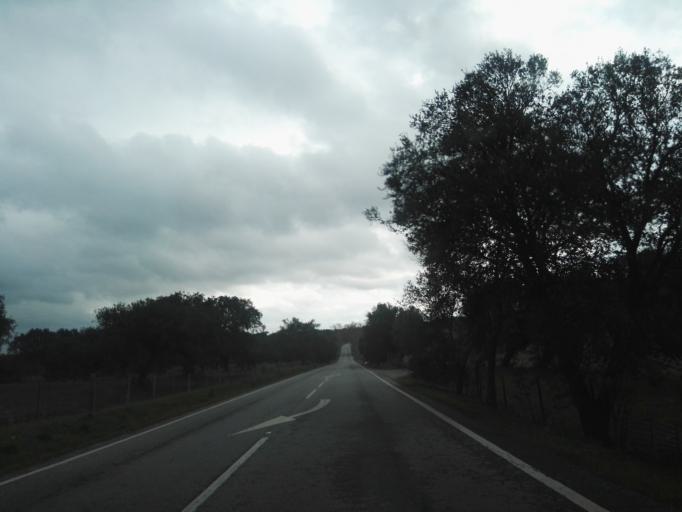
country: PT
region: Portalegre
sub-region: Arronches
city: Arronches
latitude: 39.1085
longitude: -7.2804
